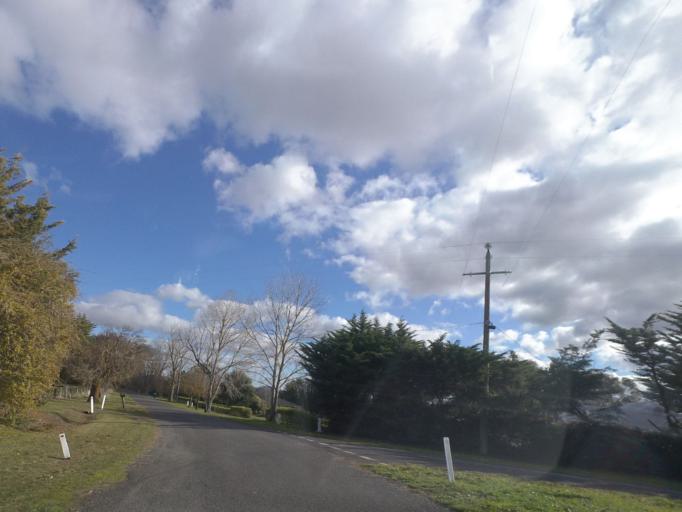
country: AU
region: Victoria
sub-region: Mount Alexander
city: Castlemaine
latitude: -37.2500
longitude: 144.3879
